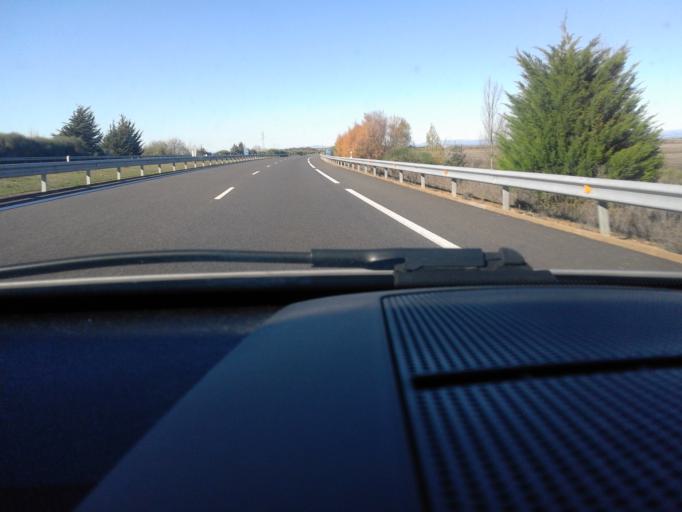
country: ES
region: Castille and Leon
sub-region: Provincia de Leon
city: Santas Martas
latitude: 42.4331
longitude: -5.3348
